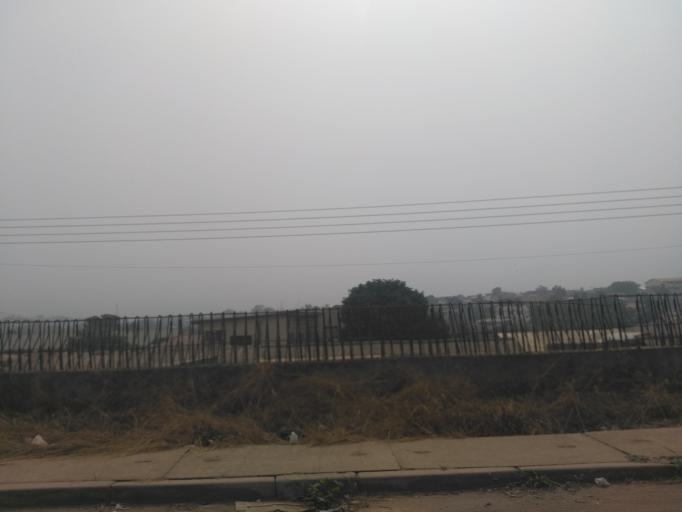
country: GH
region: Ashanti
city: Kumasi
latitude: 6.6977
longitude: -1.6397
